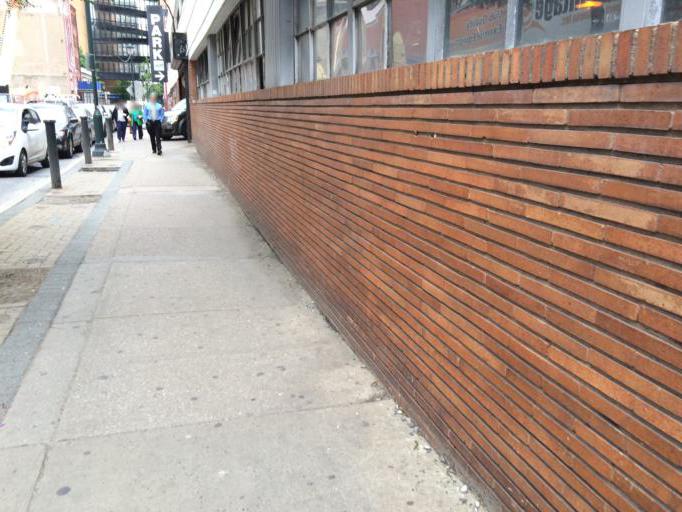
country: US
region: Pennsylvania
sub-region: Philadelphia County
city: Philadelphia
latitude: 39.9497
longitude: -75.1605
